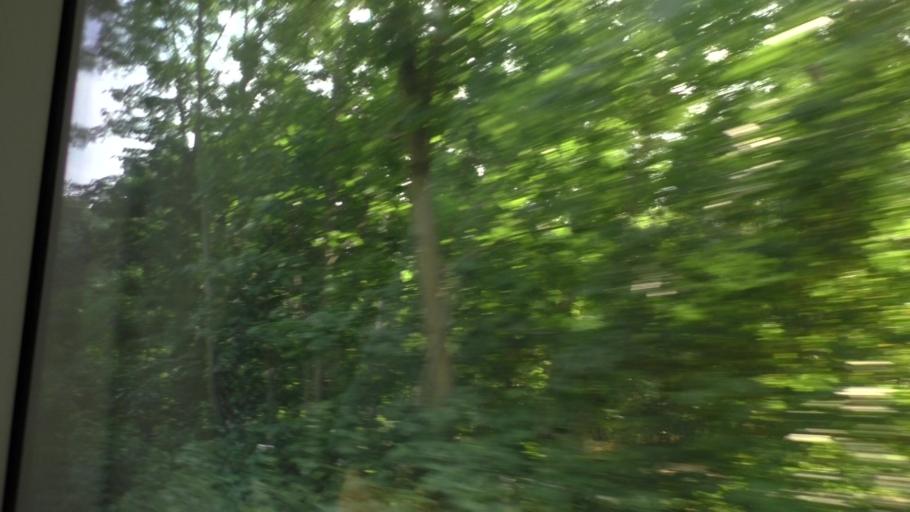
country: DE
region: Brandenburg
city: Wendisch Rietz
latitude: 52.2051
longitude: 14.0116
